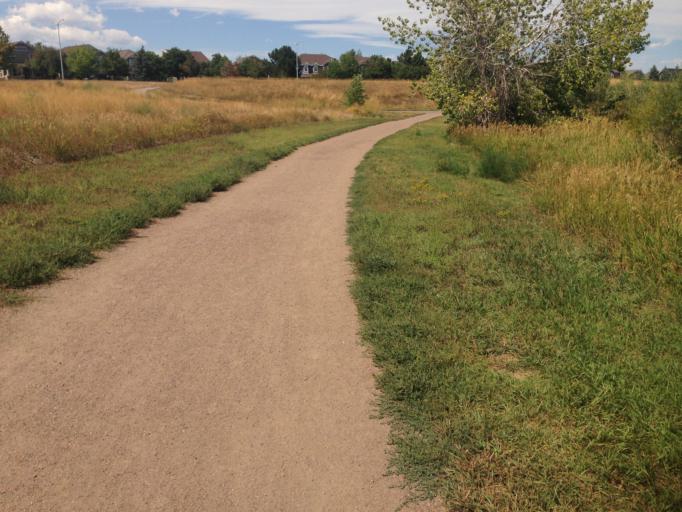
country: US
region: Colorado
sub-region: Adams County
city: Northglenn
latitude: 39.9524
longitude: -105.0164
